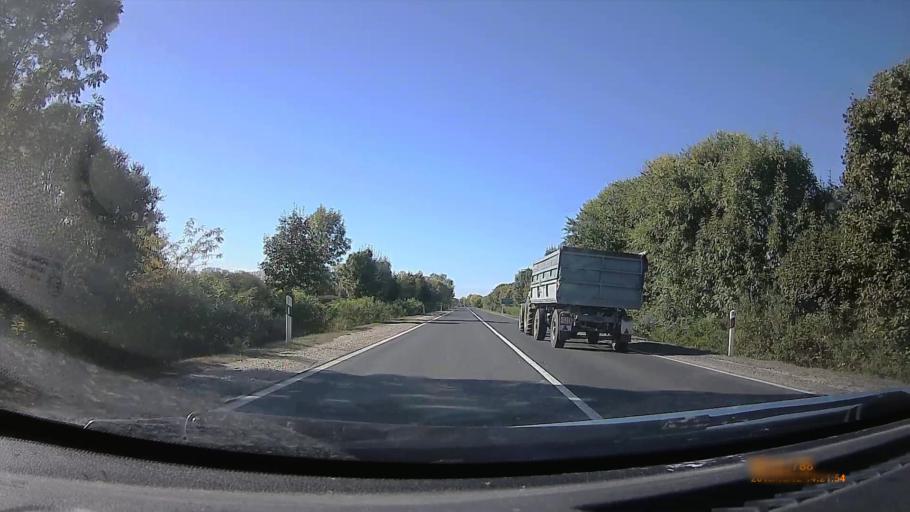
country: HU
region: Hajdu-Bihar
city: Biharkeresztes
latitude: 47.1409
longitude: 21.7250
